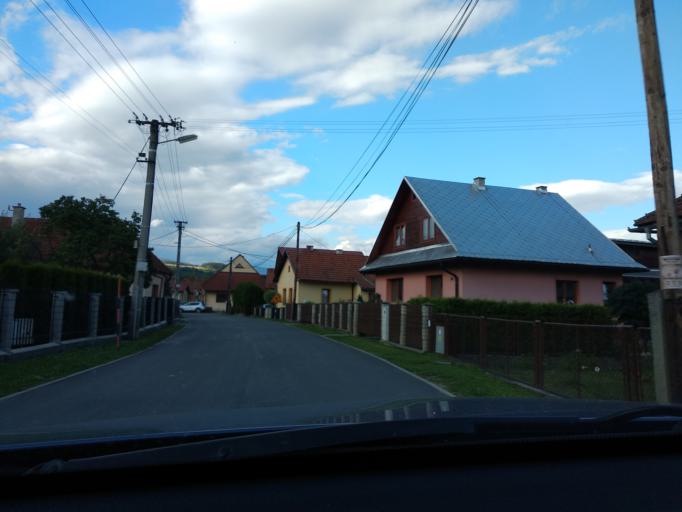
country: SK
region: Zilinsky
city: Ruzomberok
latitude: 49.0935
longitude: 19.4083
